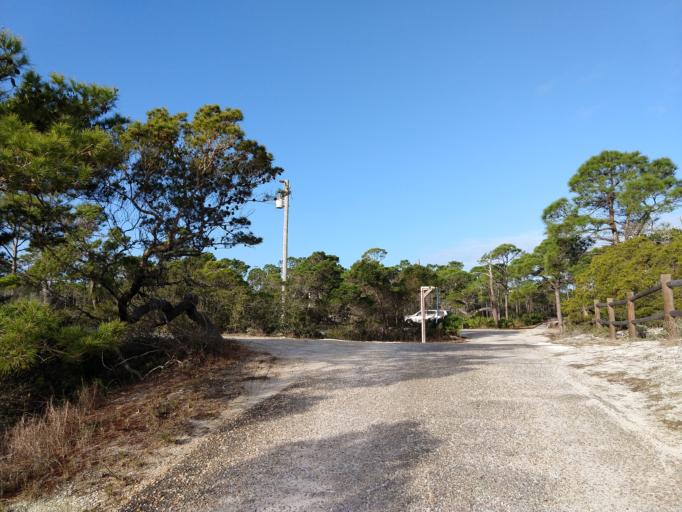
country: US
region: Florida
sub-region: Gulf County
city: Port Saint Joe
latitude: 29.7888
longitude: -85.4068
